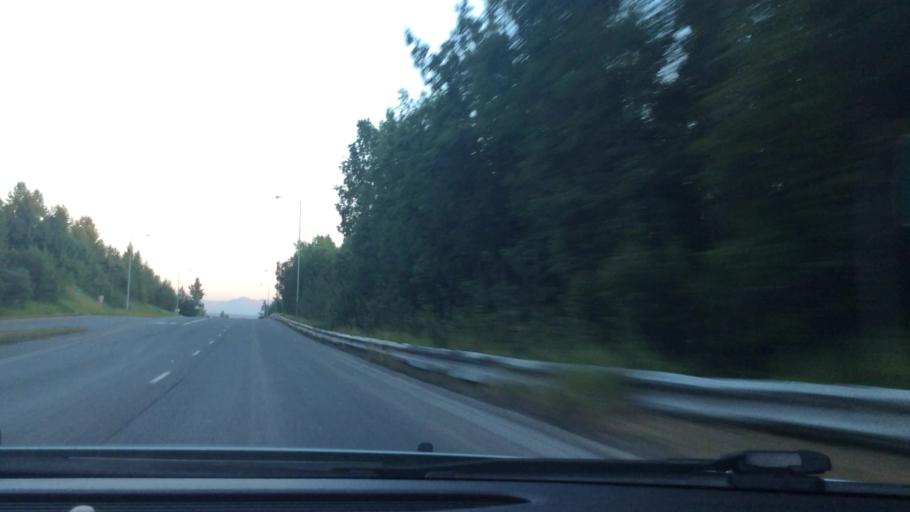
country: US
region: Alaska
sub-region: Anchorage Municipality
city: Anchorage
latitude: 61.2065
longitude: -149.7786
